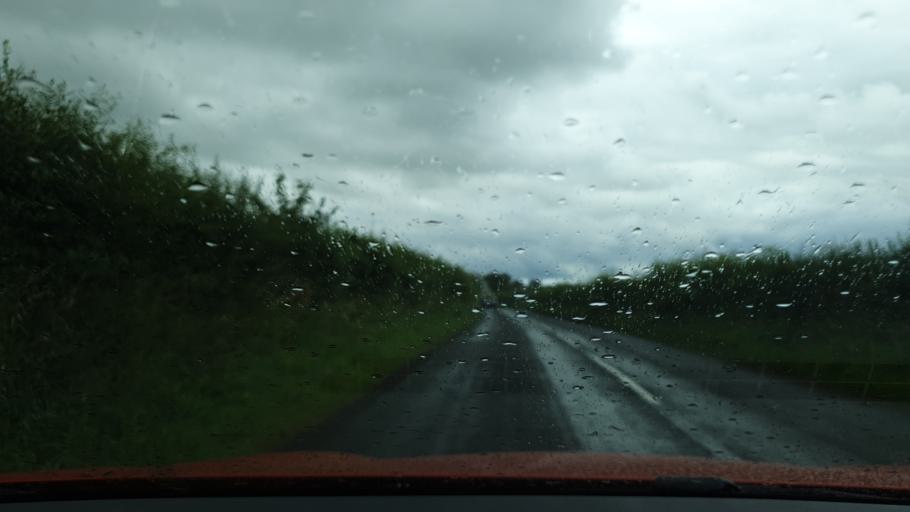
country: GB
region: England
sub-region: Cumbria
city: Penrith
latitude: 54.6258
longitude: -2.7949
